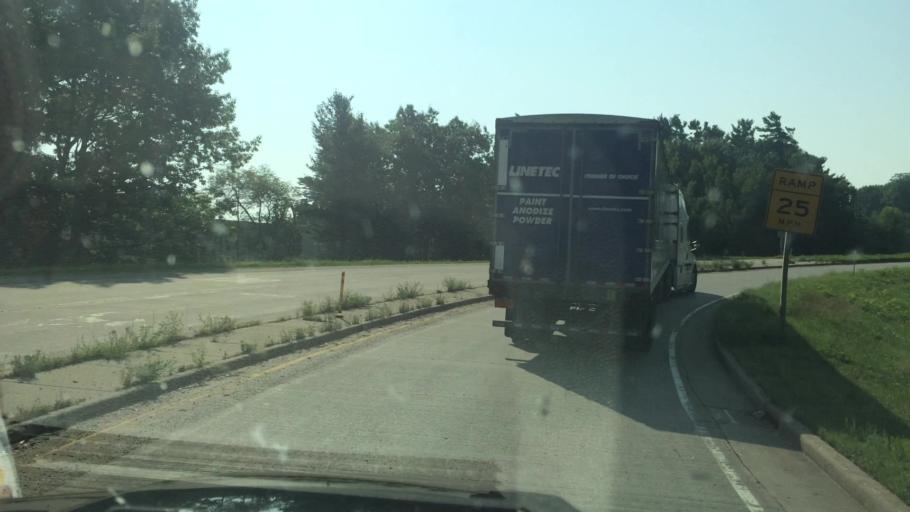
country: US
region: Wisconsin
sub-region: Marathon County
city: Rothschild
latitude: 44.8971
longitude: -89.6122
